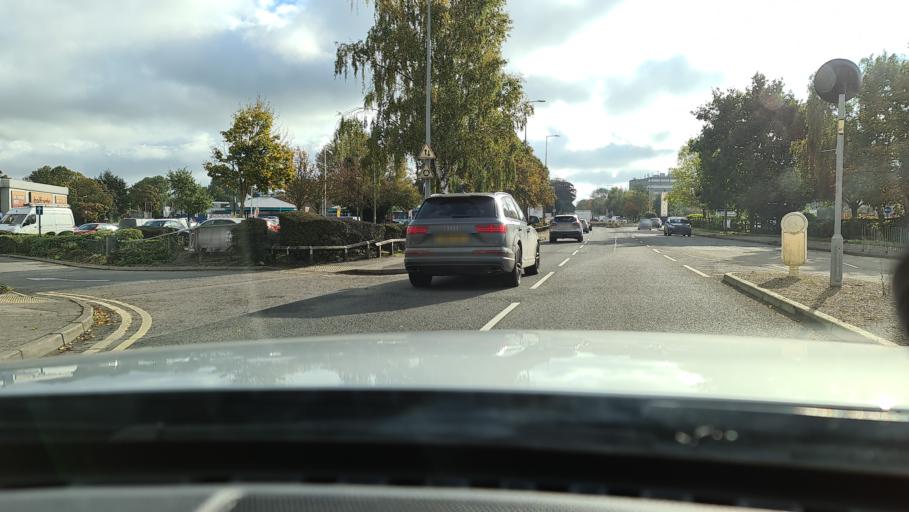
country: GB
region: England
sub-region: Buckinghamshire
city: Bletchley
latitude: 52.0022
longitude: -0.7253
